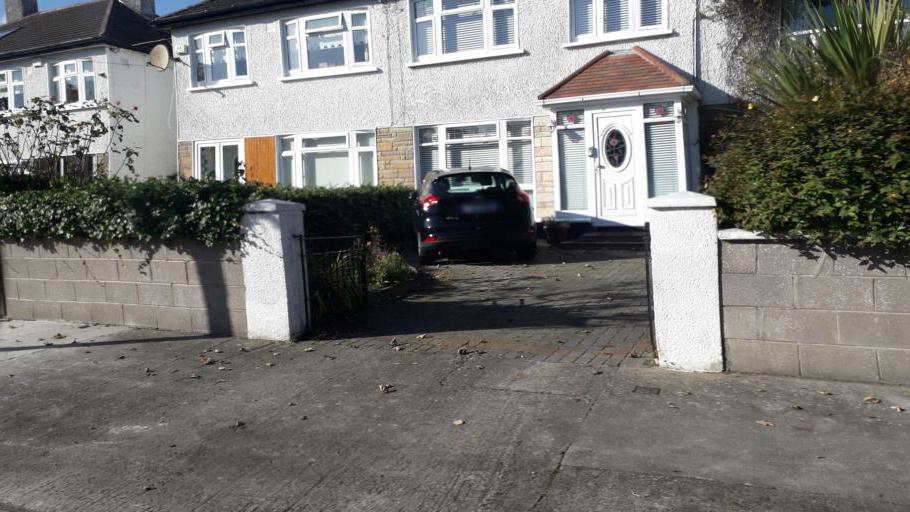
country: IE
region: Leinster
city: Raheny
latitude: 53.3888
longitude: -6.1750
